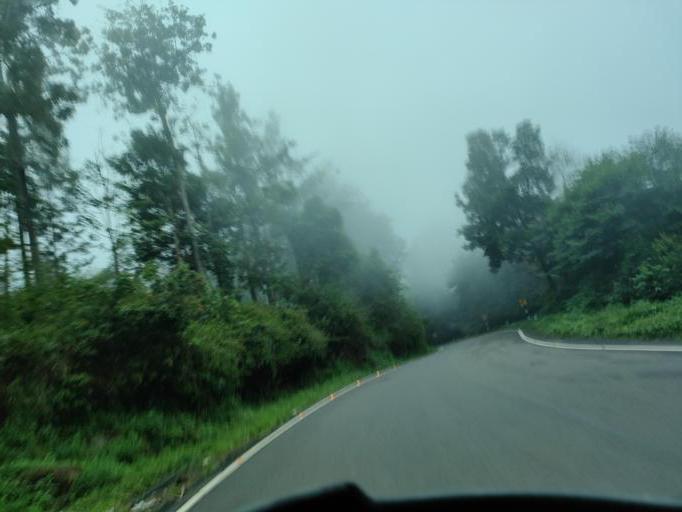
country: IN
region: Tamil Nadu
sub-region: Dindigul
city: Ayakudi
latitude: 10.3552
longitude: 77.5672
